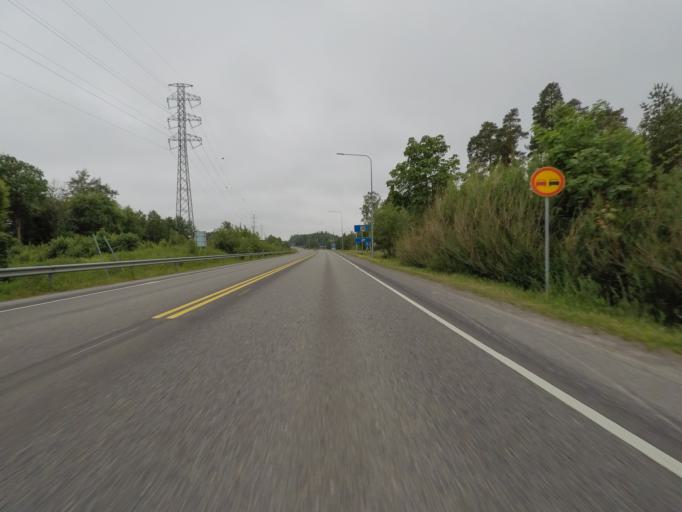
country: FI
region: Varsinais-Suomi
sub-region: Turku
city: Naantali
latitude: 60.4709
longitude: 22.0457
